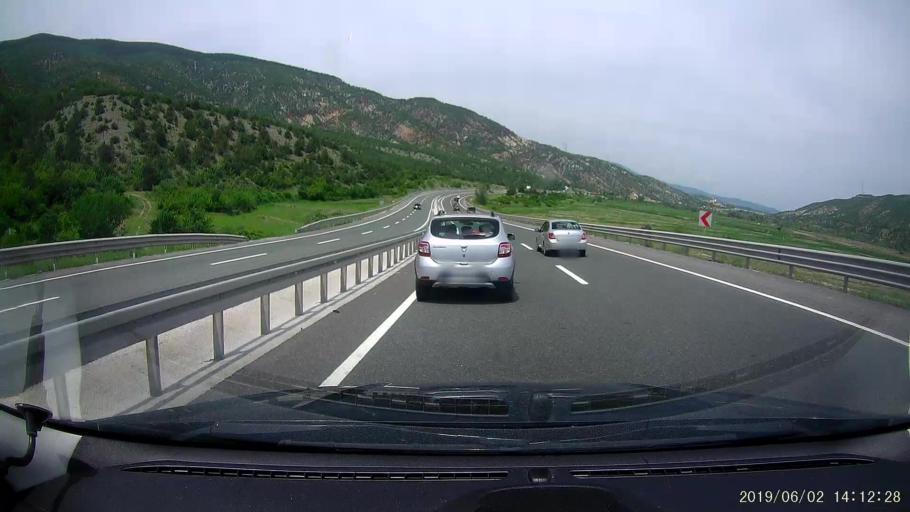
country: TR
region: Cankiri
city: Yaprakli
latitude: 40.9138
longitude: 33.8106
